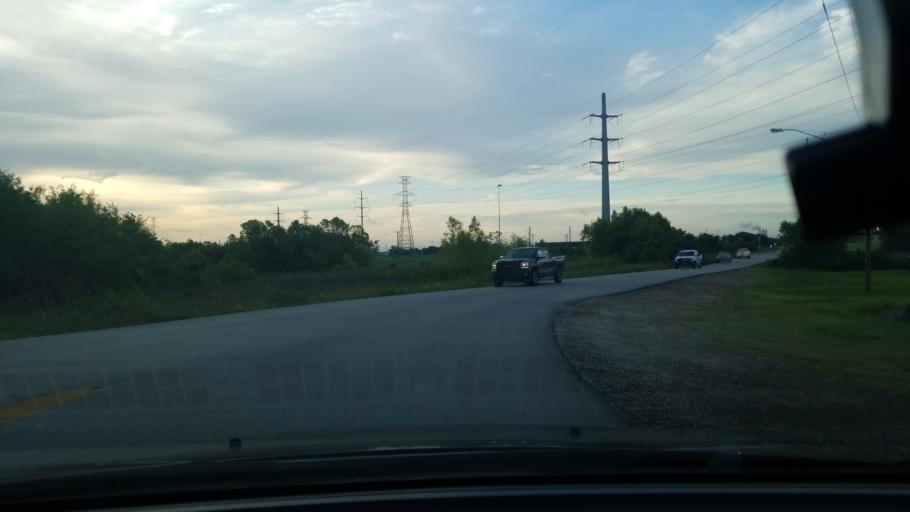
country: US
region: Texas
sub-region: Dallas County
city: Balch Springs
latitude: 32.7779
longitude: -96.6617
